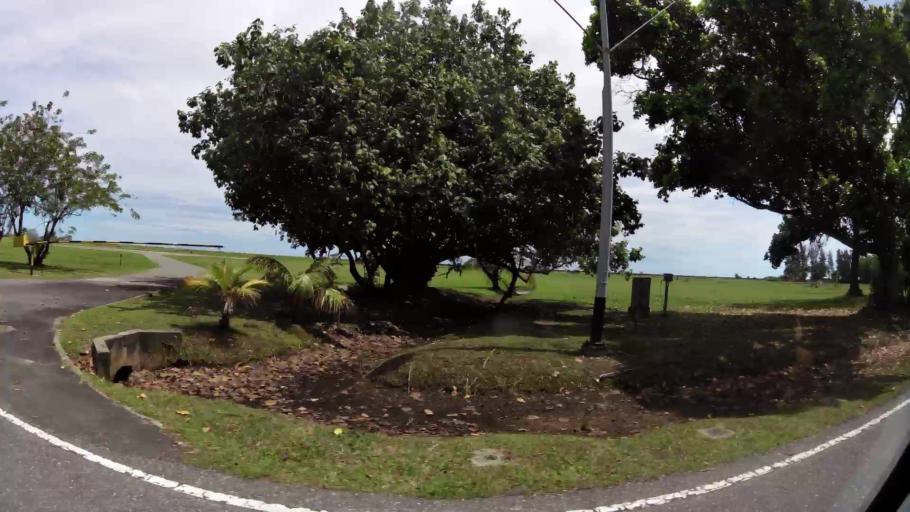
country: BN
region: Belait
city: Seria
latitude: 4.6071
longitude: 114.2923
